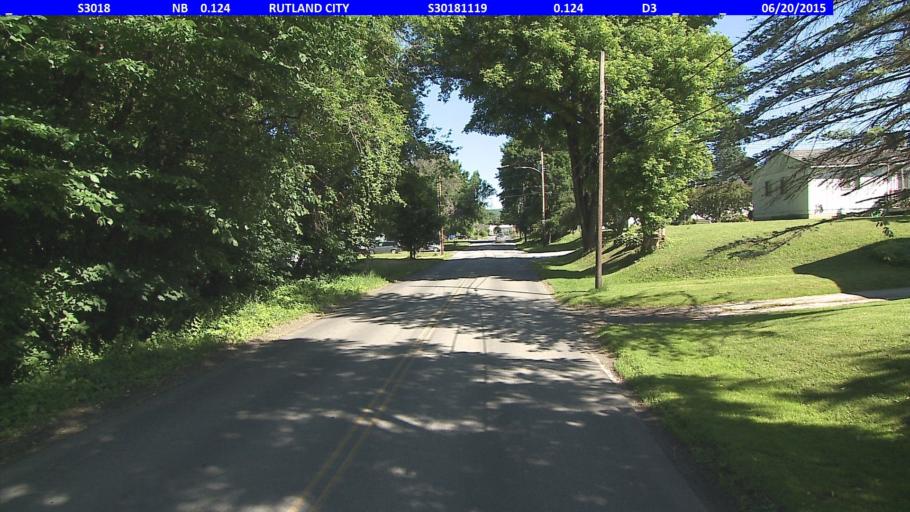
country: US
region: Vermont
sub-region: Rutland County
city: Rutland
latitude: 43.5950
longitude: -72.9817
